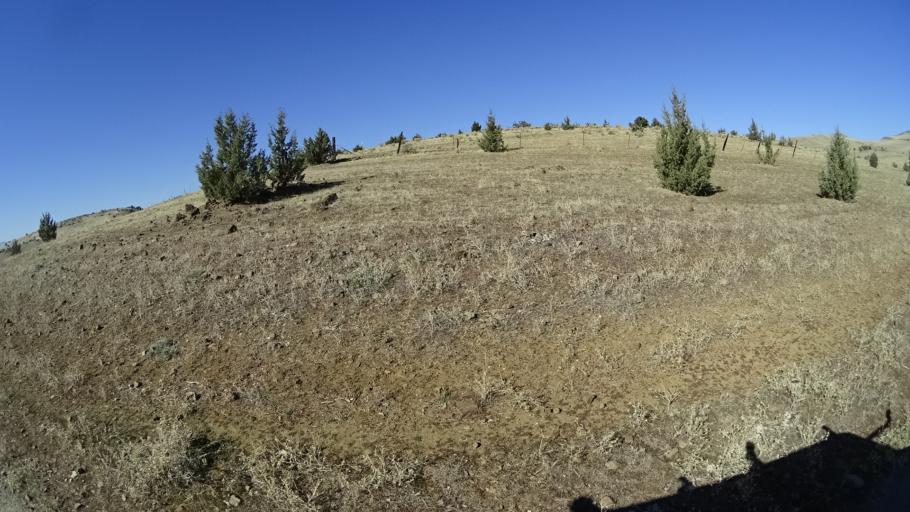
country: US
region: California
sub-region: Siskiyou County
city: Montague
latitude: 41.7402
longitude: -122.3345
